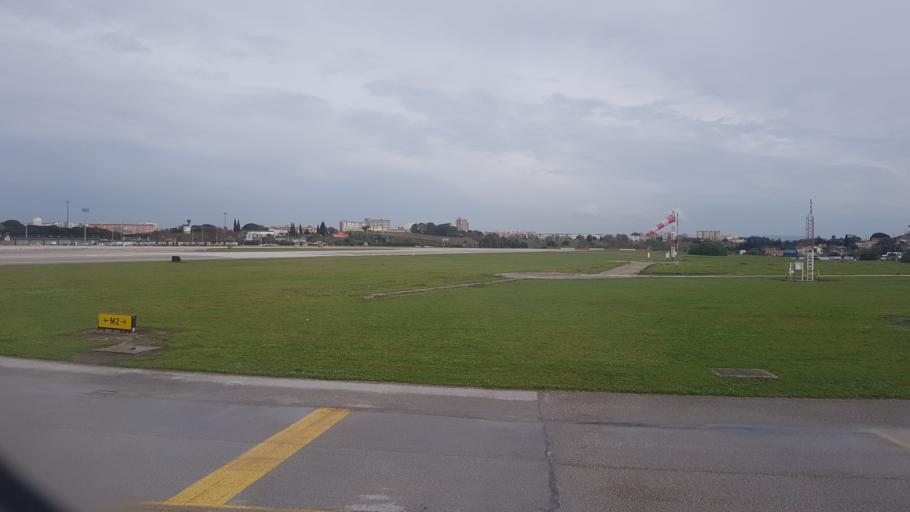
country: PT
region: Lisbon
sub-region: Loures
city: Moscavide
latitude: 38.7674
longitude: -9.1339
